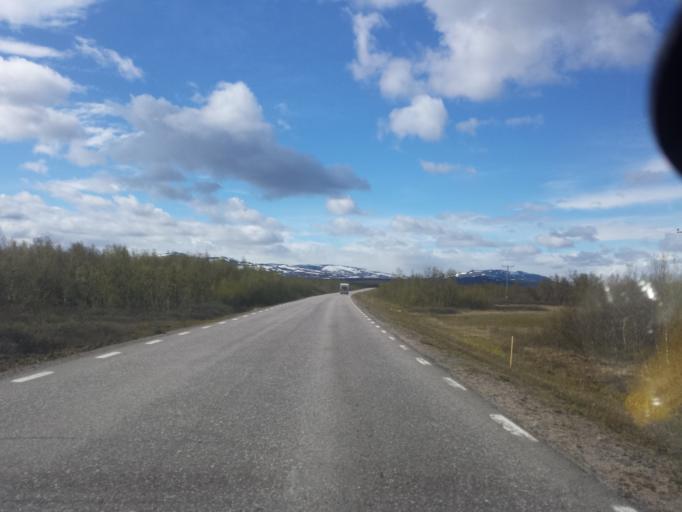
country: SE
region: Norrbotten
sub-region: Kiruna Kommun
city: Kiruna
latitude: 67.9988
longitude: 19.8652
